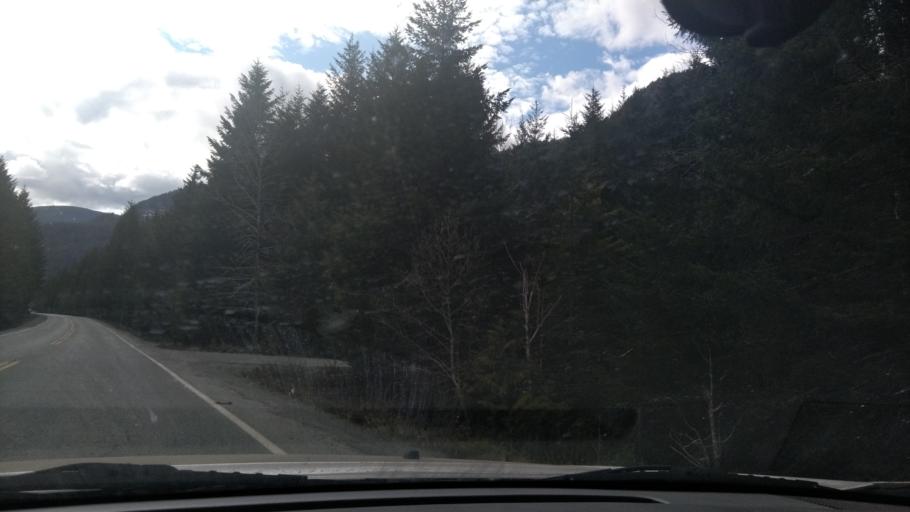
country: CA
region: British Columbia
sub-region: Regional District of Alberni-Clayoquot
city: Tofino
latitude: 49.8346
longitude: -125.9533
